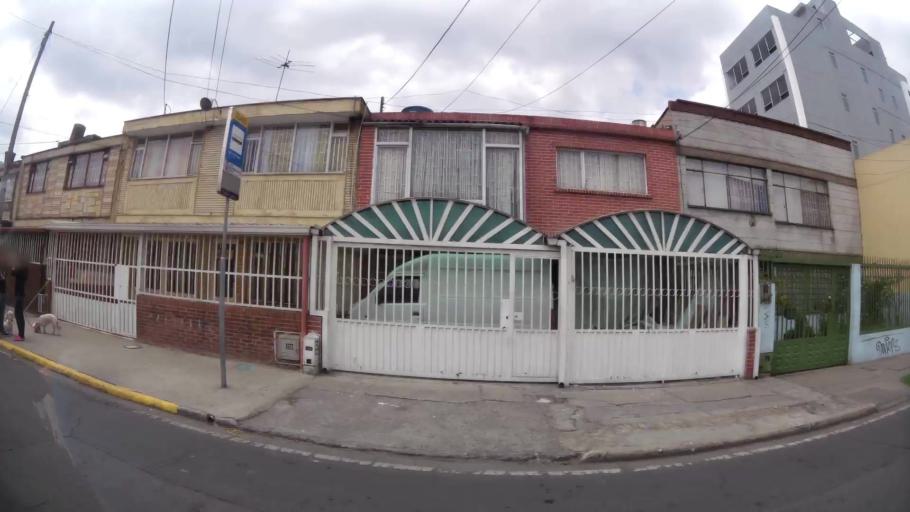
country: CO
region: Bogota D.C.
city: Bogota
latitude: 4.6004
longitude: -74.1031
